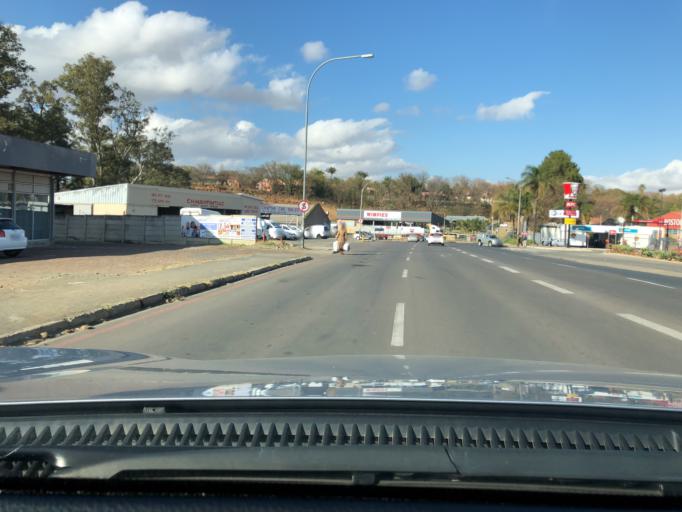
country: ZA
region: KwaZulu-Natal
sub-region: uThukela District Municipality
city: Ladysmith
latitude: -28.5561
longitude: 29.7729
